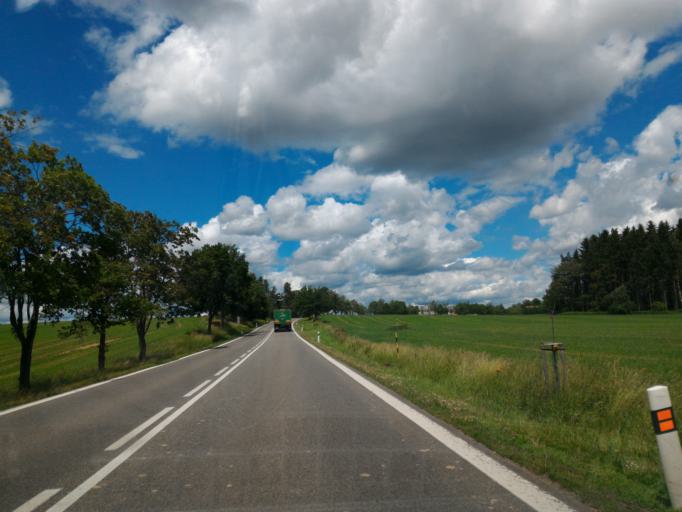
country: CZ
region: Vysocina
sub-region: Okres Zd'ar nad Sazavou
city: Nove Veseli
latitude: 49.5281
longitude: 15.9091
